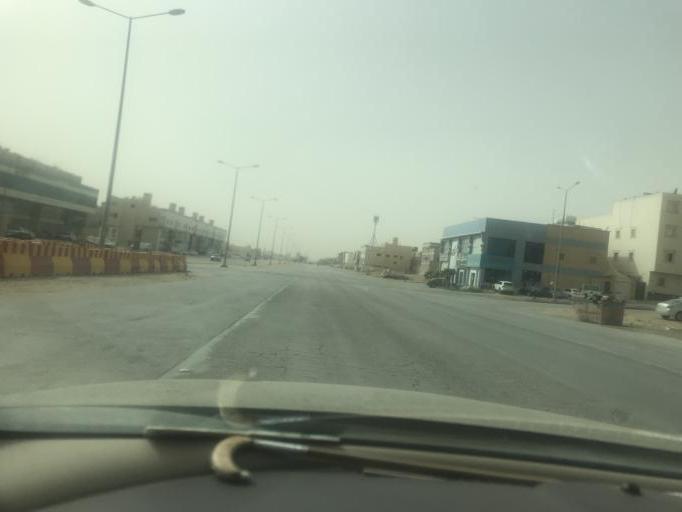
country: SA
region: Ar Riyad
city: Riyadh
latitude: 24.8072
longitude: 46.6021
